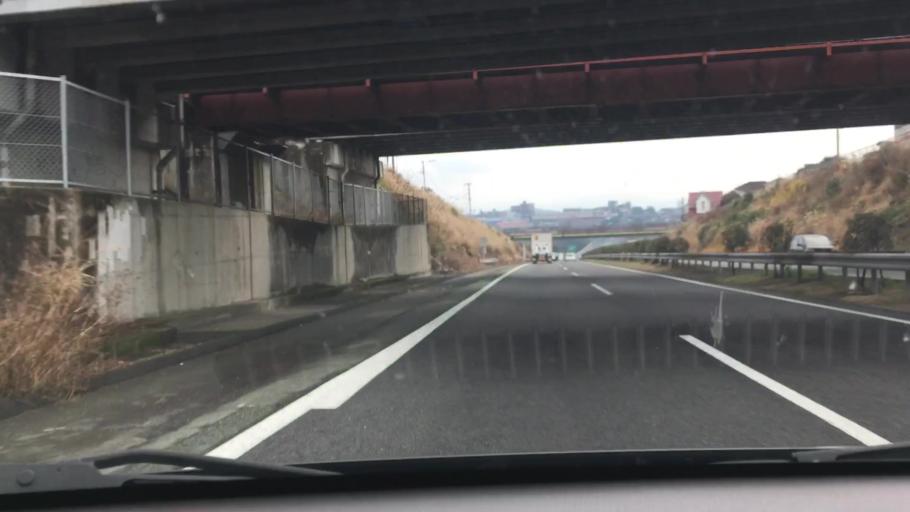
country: JP
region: Kumamoto
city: Kumamoto
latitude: 32.8484
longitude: 130.7678
